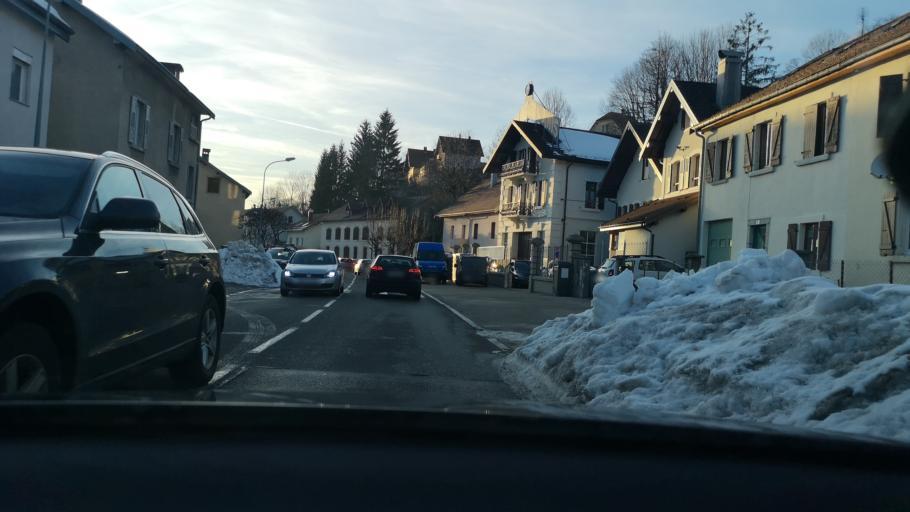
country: FR
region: Franche-Comte
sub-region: Departement du Doubs
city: Pontarlier
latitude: 46.9058
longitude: 6.3651
